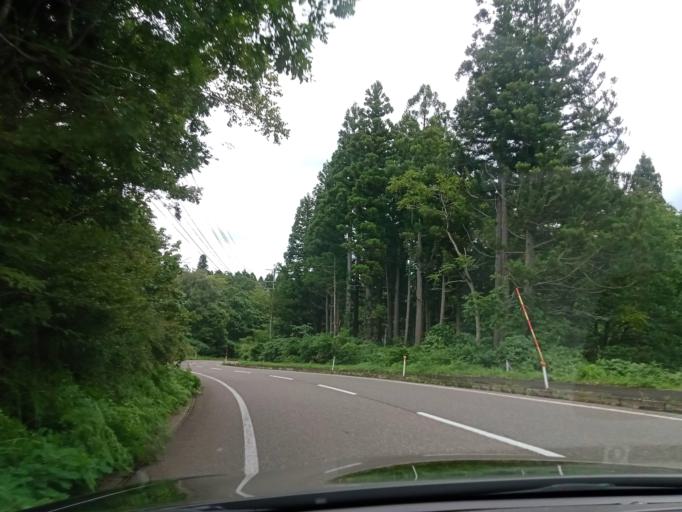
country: JP
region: Niigata
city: Arai
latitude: 36.8783
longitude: 138.1902
